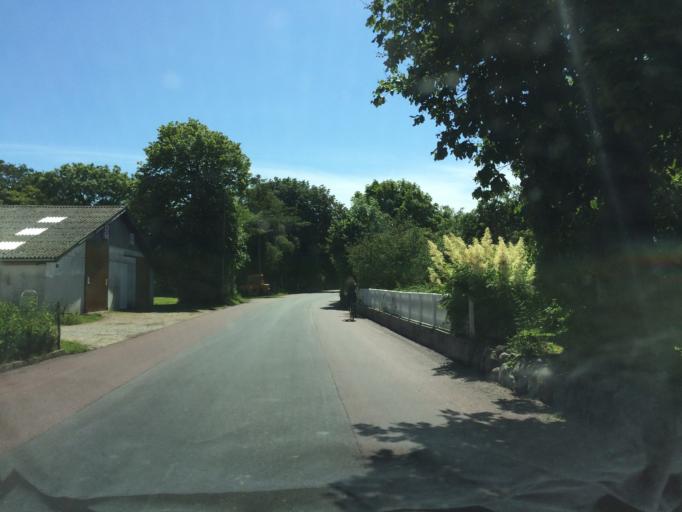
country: DK
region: Central Jutland
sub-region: Samso Kommune
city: Tranebjerg
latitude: 55.8174
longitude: 10.6052
